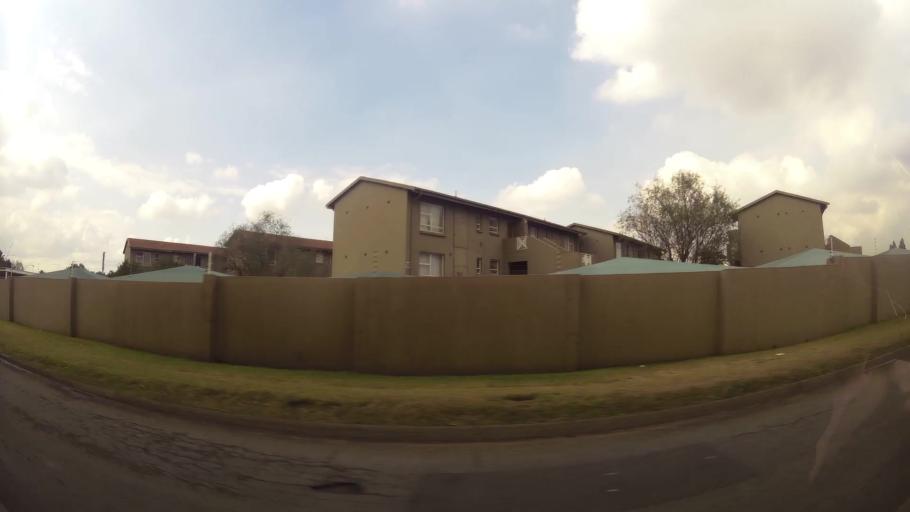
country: ZA
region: Gauteng
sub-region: Sedibeng District Municipality
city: Vereeniging
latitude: -26.6715
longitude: 27.9390
